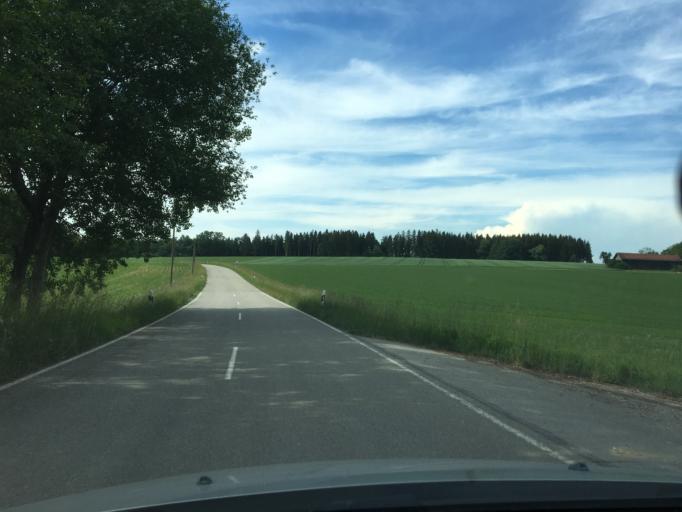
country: DE
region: Bavaria
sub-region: Upper Bavaria
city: Niedertaufkirchen
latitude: 48.3719
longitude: 12.5697
